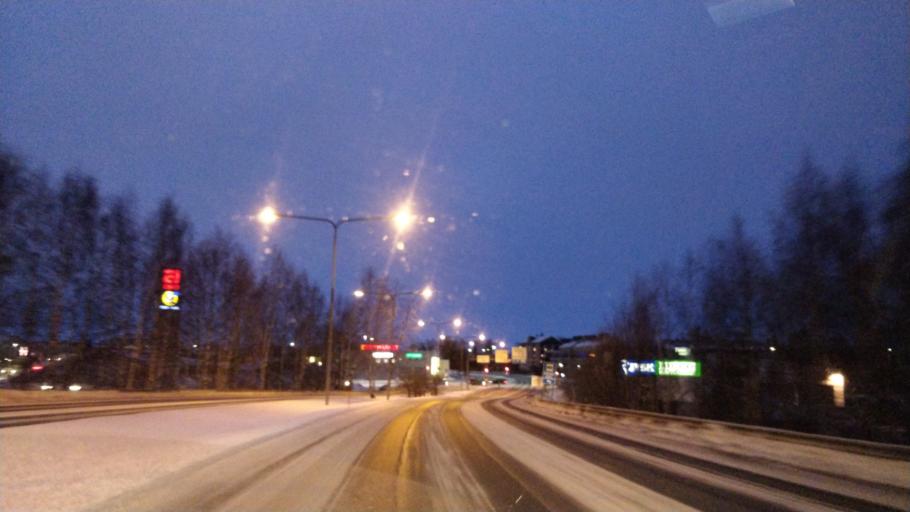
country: FI
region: Lapland
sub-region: Kemi-Tornio
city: Kemi
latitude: 65.7408
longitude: 24.5692
